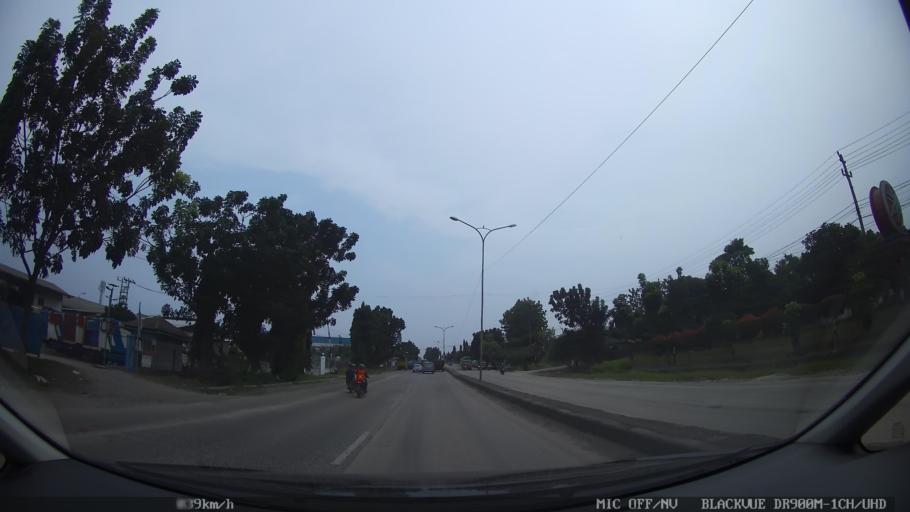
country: ID
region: Lampung
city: Bandarlampung
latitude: -5.4198
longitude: 105.2955
